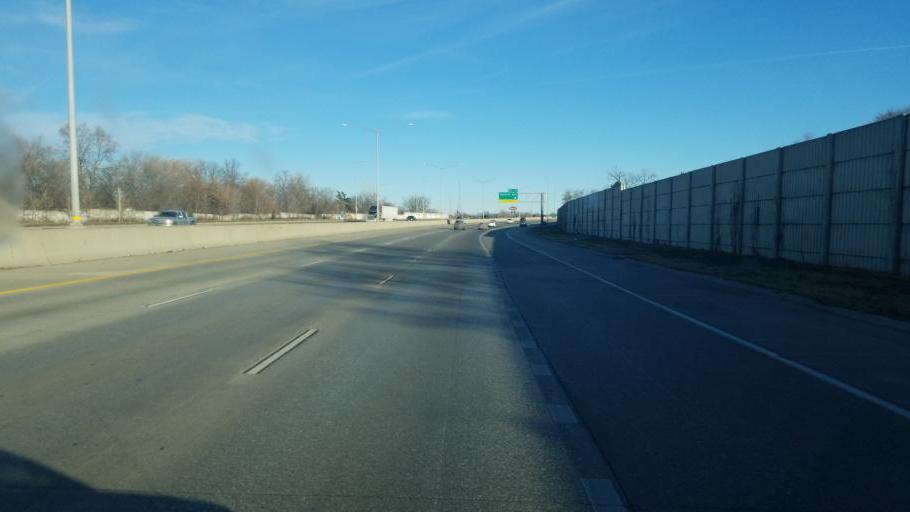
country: US
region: Iowa
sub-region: Polk County
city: Des Moines
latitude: 41.6096
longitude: -93.5786
